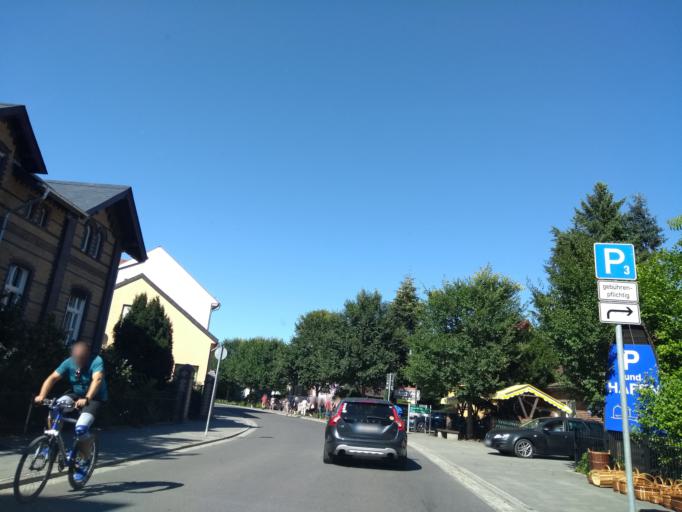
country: DE
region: Brandenburg
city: Lubbenau
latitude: 51.8652
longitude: 13.9734
